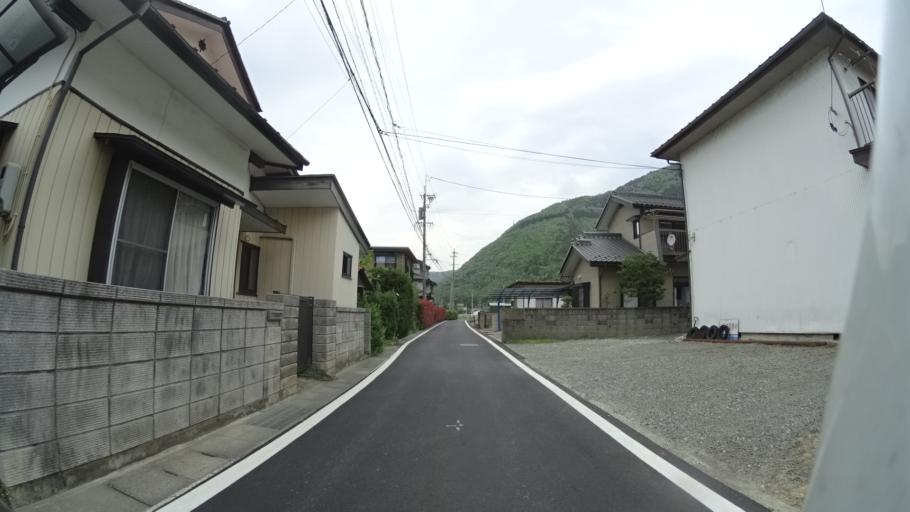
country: JP
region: Nagano
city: Ueda
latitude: 36.4916
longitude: 138.1540
